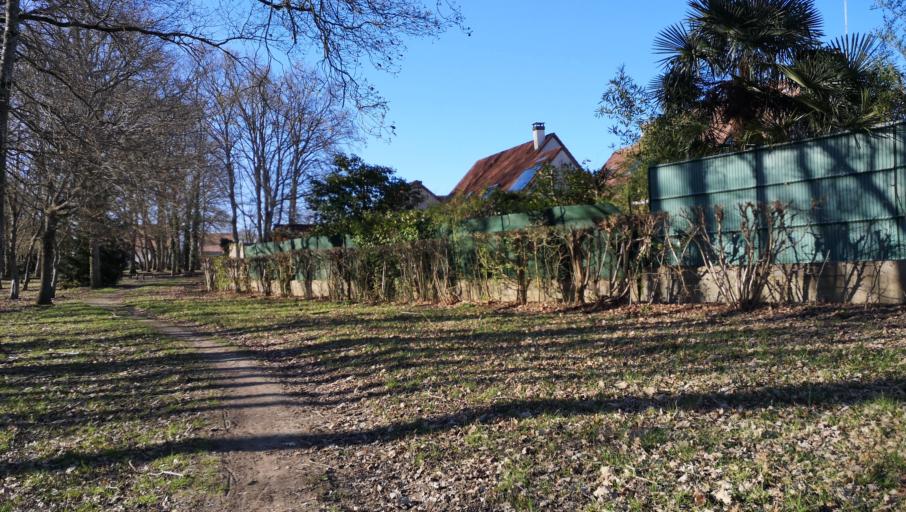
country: FR
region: Centre
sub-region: Departement du Loiret
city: Saint-Jean-de-Braye
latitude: 47.9140
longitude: 1.9935
